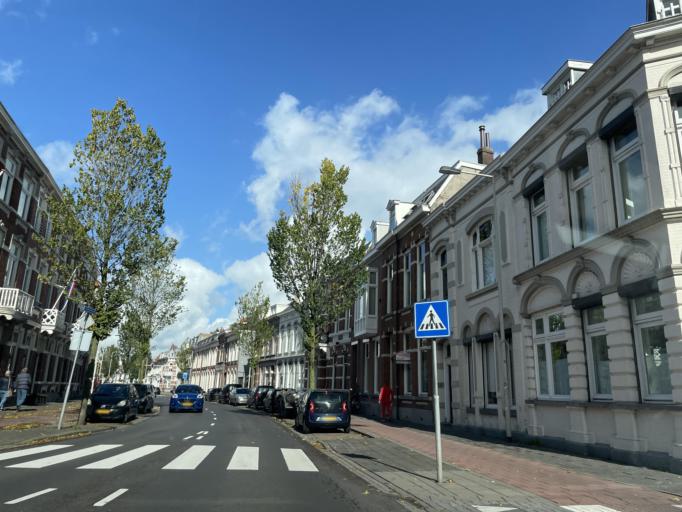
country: NL
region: North Brabant
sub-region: Gemeente Bergen op Zoom
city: Bergen op Zoom
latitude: 51.4904
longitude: 4.2893
